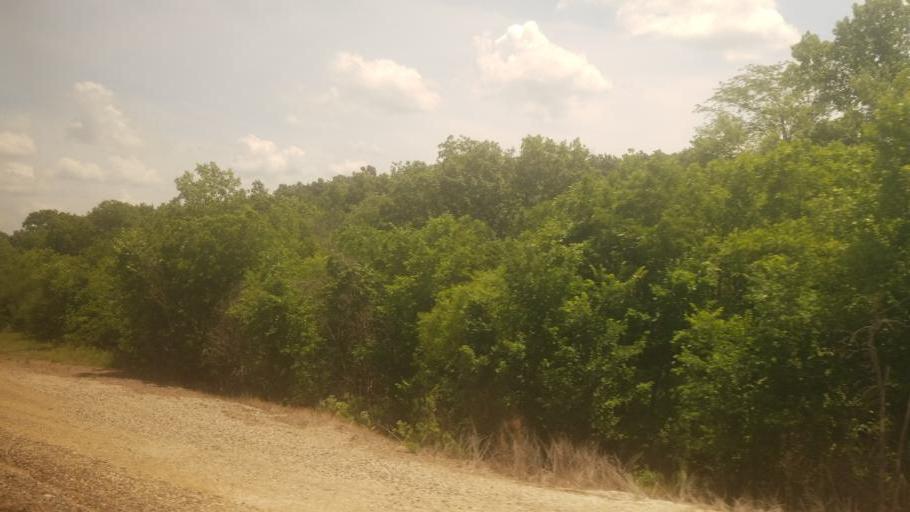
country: US
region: Missouri
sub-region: Macon County
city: La Plata
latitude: 40.0743
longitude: -92.4401
